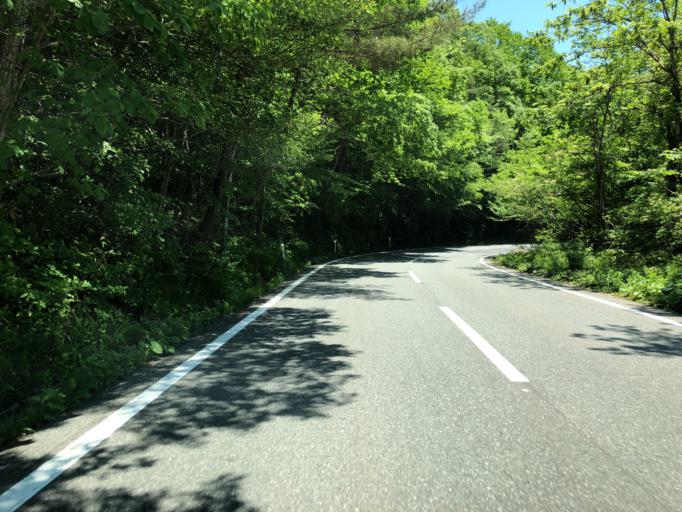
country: JP
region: Fukushima
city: Namie
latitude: 37.5166
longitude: 140.8303
